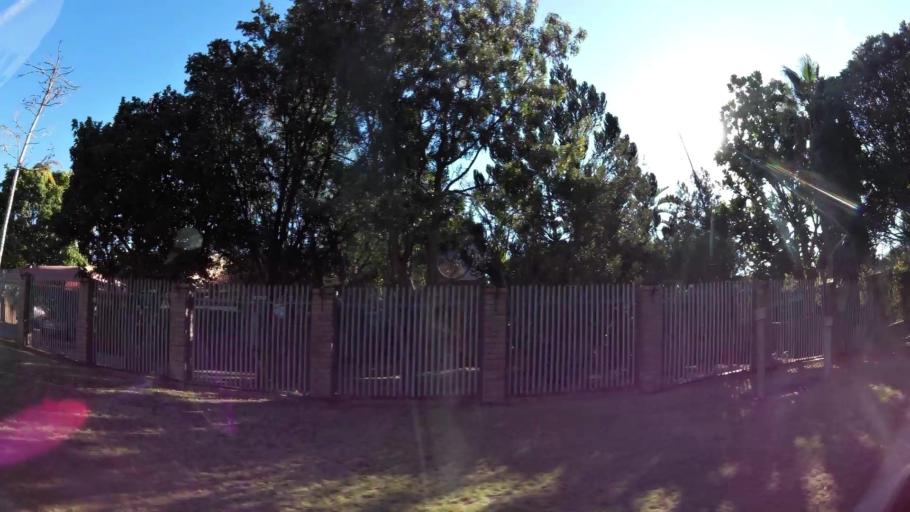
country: ZA
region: Limpopo
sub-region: Capricorn District Municipality
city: Polokwane
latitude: -23.8855
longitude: 29.4888
